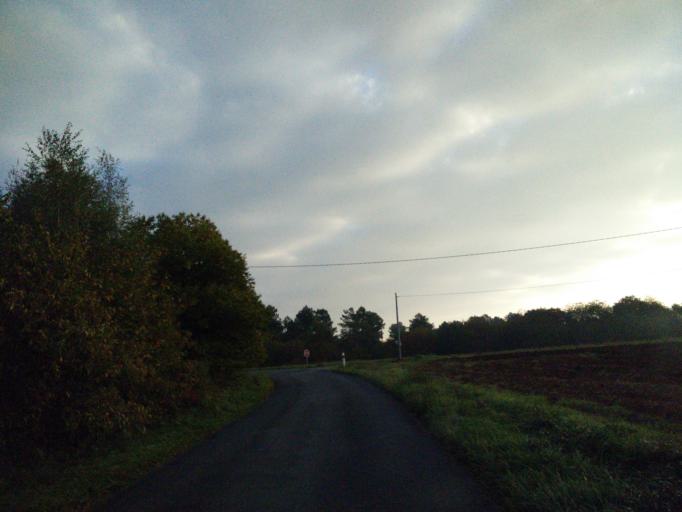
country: FR
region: Aquitaine
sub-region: Departement de la Dordogne
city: Rouffignac-Saint-Cernin-de-Reilhac
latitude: 45.0146
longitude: 0.9661
